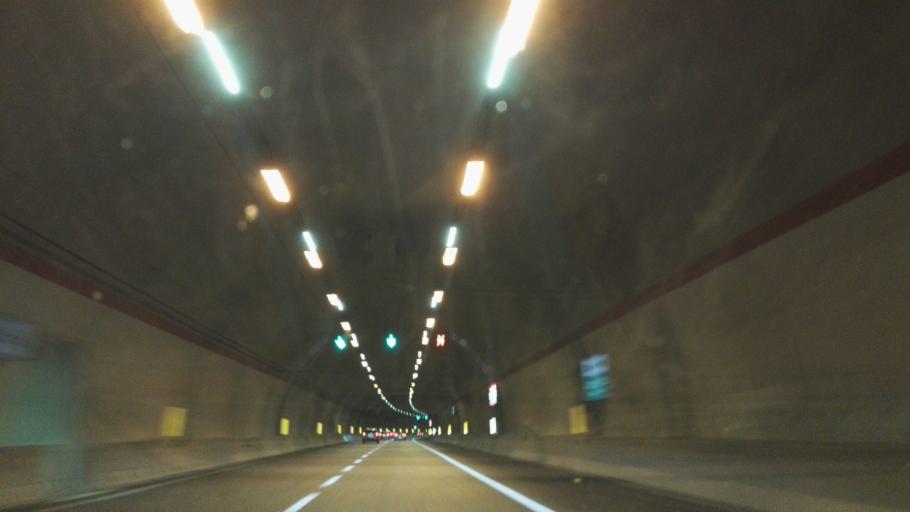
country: IT
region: Calabria
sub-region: Provincia di Catanzaro
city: Nocera Scalo
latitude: 39.0244
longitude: 16.1243
